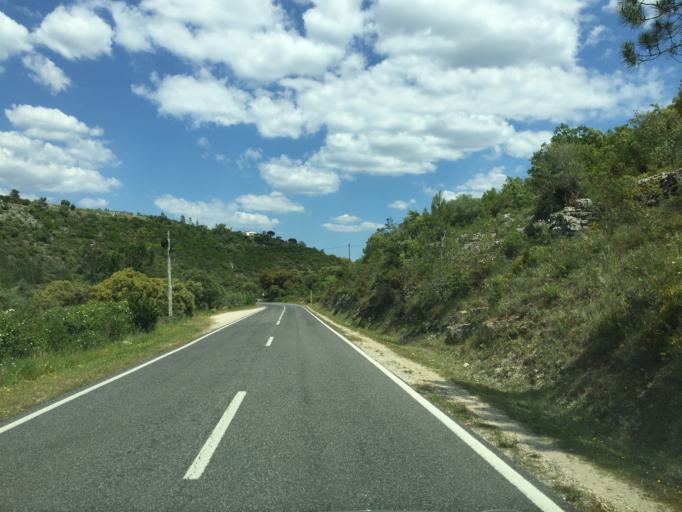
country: PT
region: Santarem
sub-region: Ourem
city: Fatima
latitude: 39.6410
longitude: -8.6377
